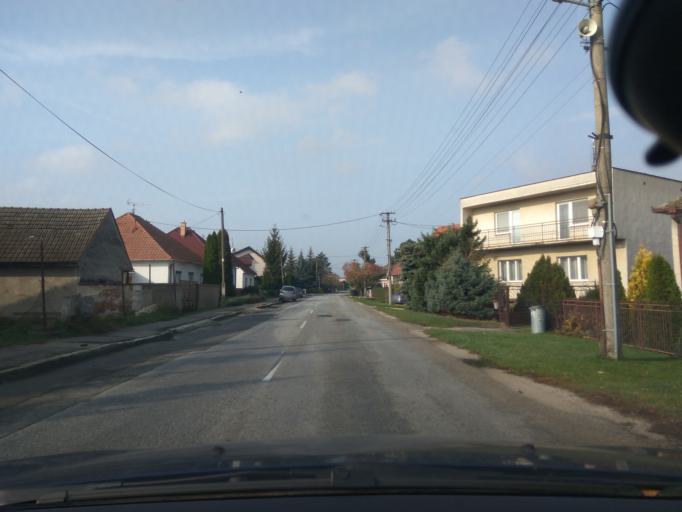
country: SK
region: Trnavsky
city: Vrbove
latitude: 48.6269
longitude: 17.7766
